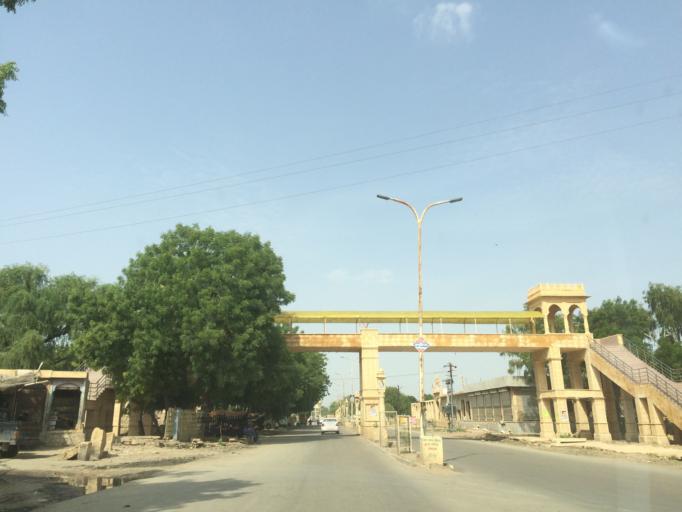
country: IN
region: Rajasthan
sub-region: Jaisalmer
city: Jaisalmer
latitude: 26.9095
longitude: 70.9171
